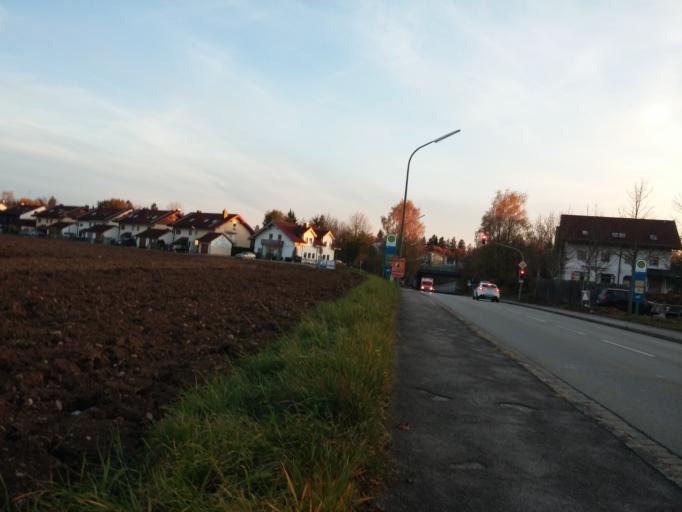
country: DE
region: Bavaria
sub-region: Upper Bavaria
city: Vaterstetten
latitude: 48.1041
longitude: 11.7713
